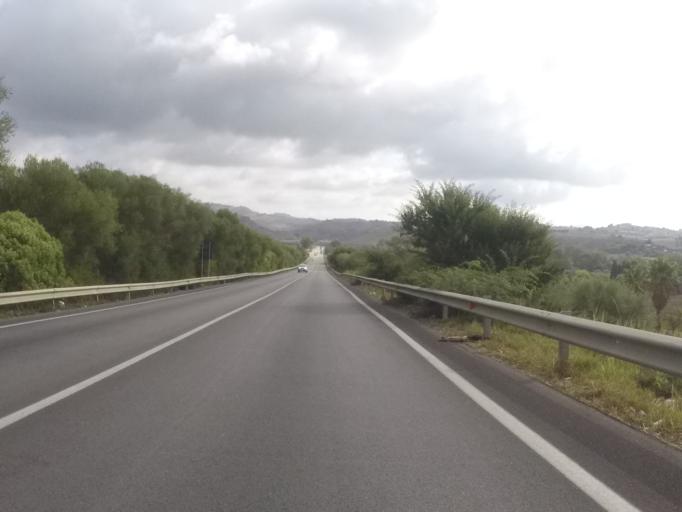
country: IT
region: Sicily
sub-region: Agrigento
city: Villaseta
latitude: 37.2776
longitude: 13.5780
